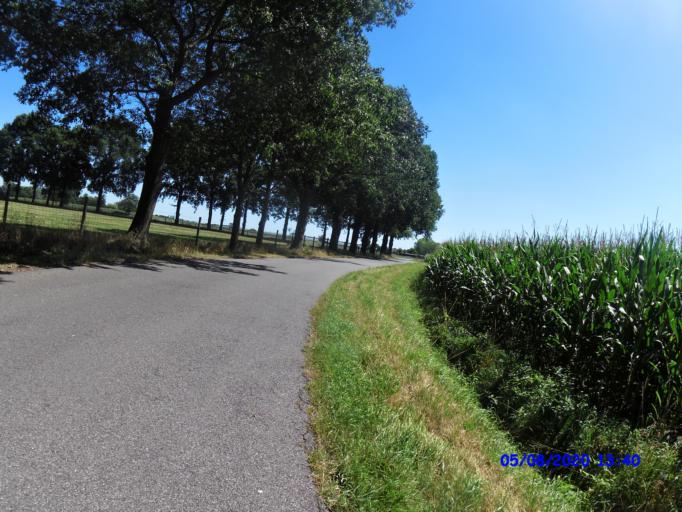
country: BE
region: Flanders
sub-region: Provincie Antwerpen
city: Rijkevorsel
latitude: 51.3599
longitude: 4.7706
